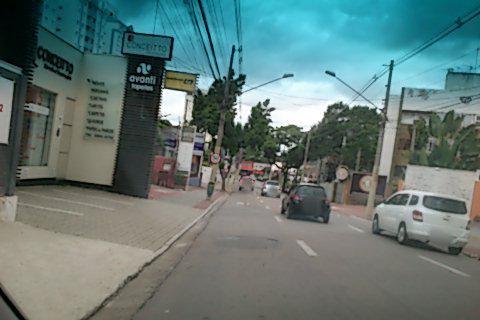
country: BR
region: Sao Paulo
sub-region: Sao Jose Dos Campos
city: Sao Jose dos Campos
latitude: -23.2032
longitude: -45.8992
